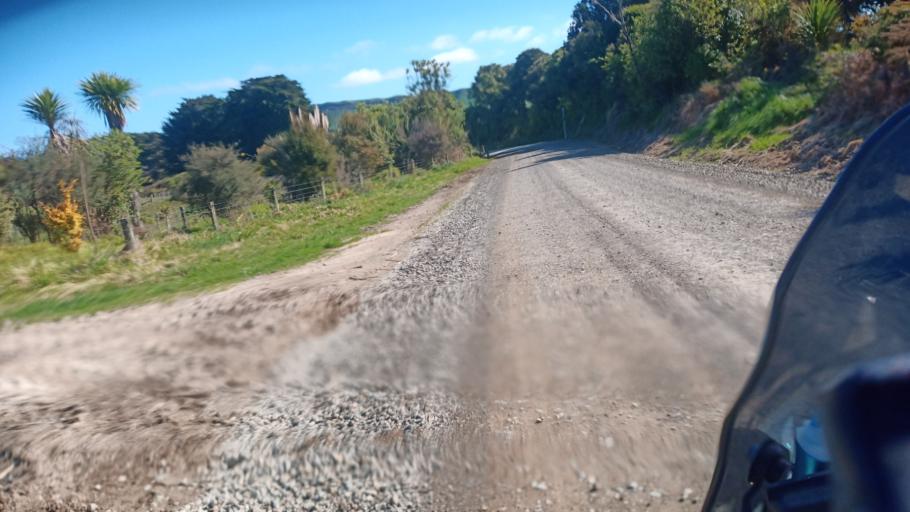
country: NZ
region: Gisborne
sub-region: Gisborne District
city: Gisborne
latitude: -39.1419
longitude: 177.9262
